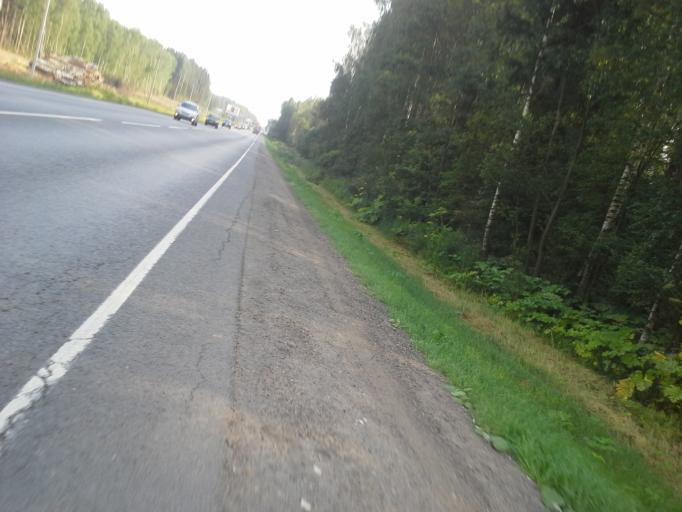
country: RU
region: Moskovskaya
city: Istra
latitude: 55.9135
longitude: 36.9453
